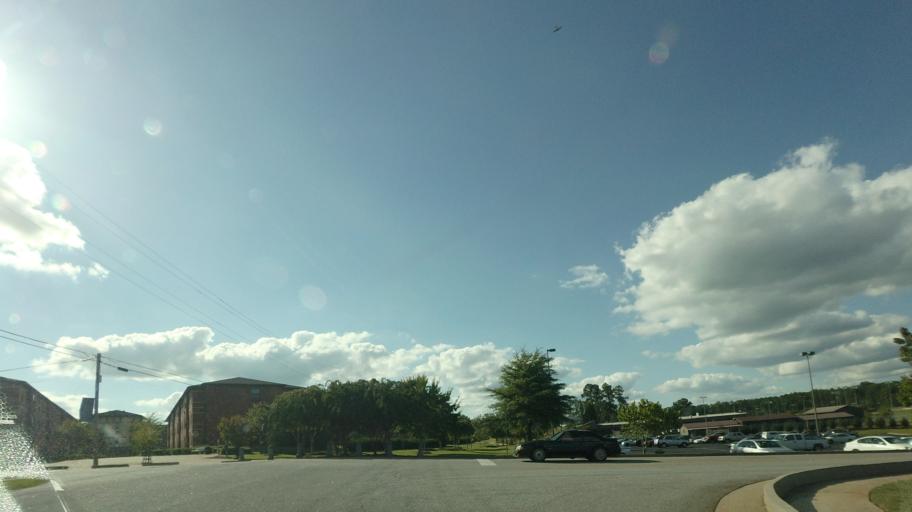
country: US
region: Georgia
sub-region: Lamar County
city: Barnesville
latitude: 33.0448
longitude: -84.1489
